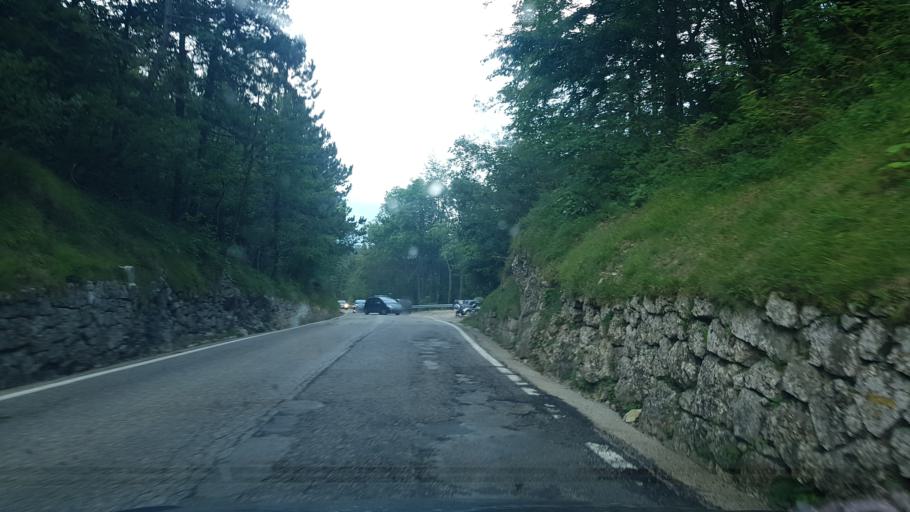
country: IT
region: Trentino-Alto Adige
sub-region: Provincia di Trento
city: Vallarsa
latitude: 45.7577
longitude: 11.1808
